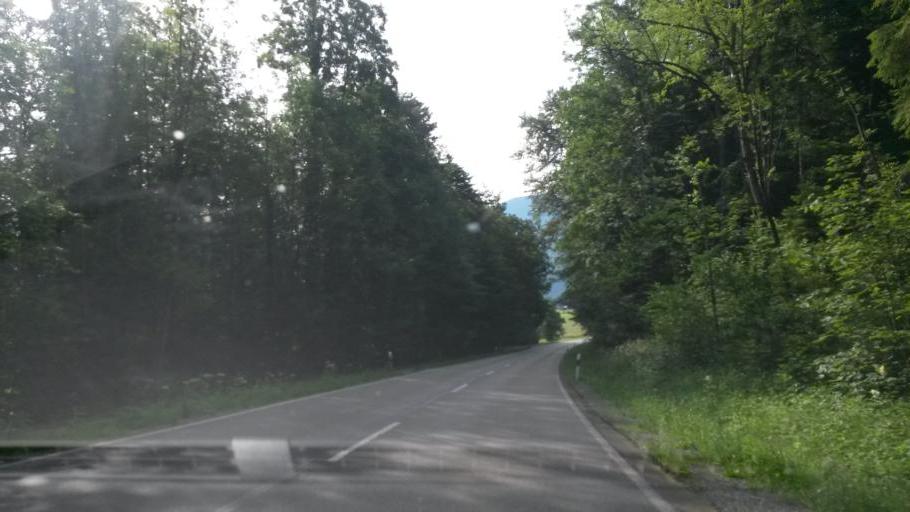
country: DE
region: Bavaria
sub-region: Upper Bavaria
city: Aschau im Chiemgau
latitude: 47.7926
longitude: 12.3073
